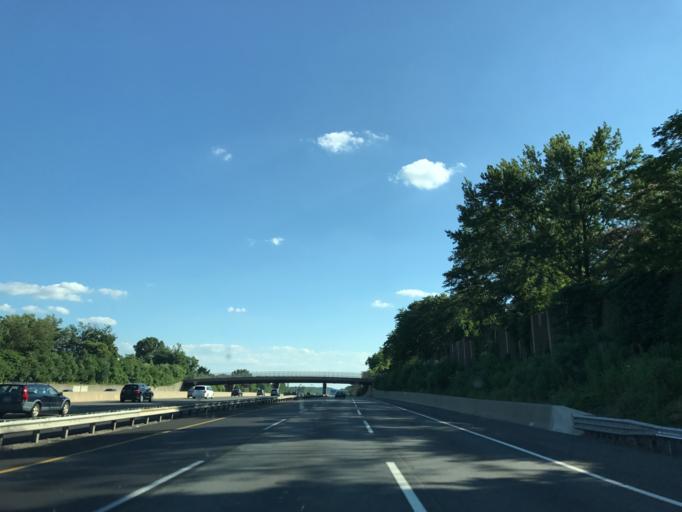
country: US
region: New Jersey
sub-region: Middlesex County
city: Milltown
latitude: 40.4646
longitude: -74.4146
